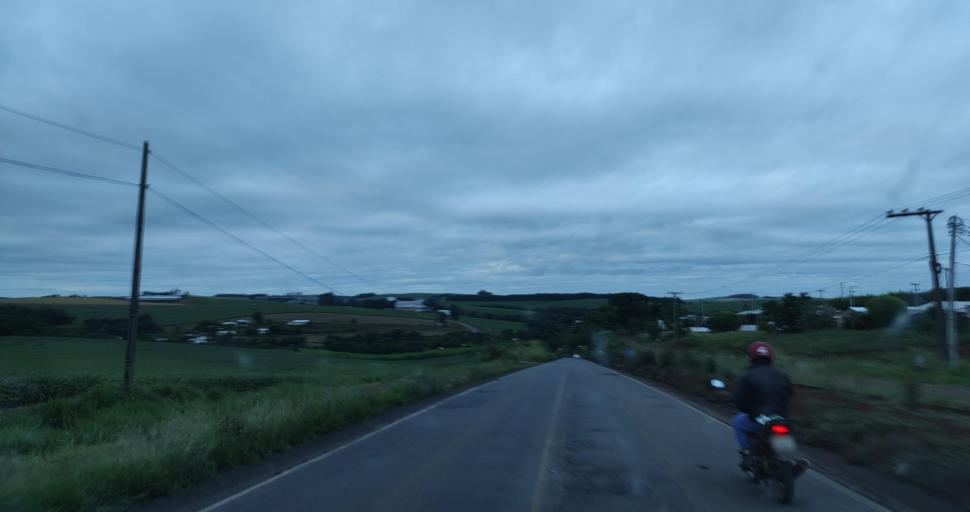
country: BR
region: Santa Catarina
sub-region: Xanxere
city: Xanxere
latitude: -26.7447
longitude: -52.3972
